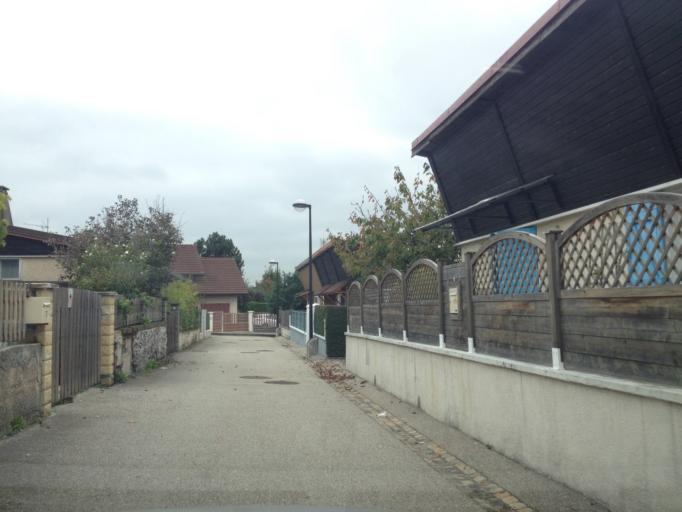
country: FR
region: Rhone-Alpes
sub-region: Departement de la Haute-Savoie
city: Seynod
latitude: 45.8918
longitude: 6.0918
